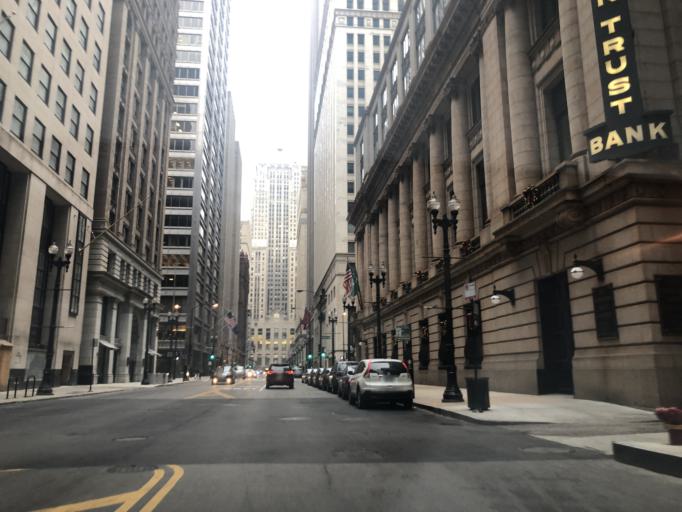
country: US
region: Illinois
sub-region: Cook County
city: Chicago
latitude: 41.8815
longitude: -87.6325
